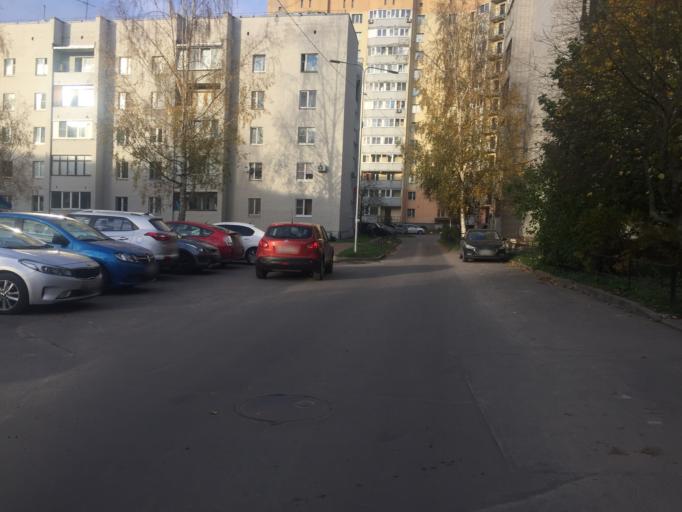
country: RU
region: Leningrad
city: Murino
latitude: 60.0465
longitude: 30.4666
